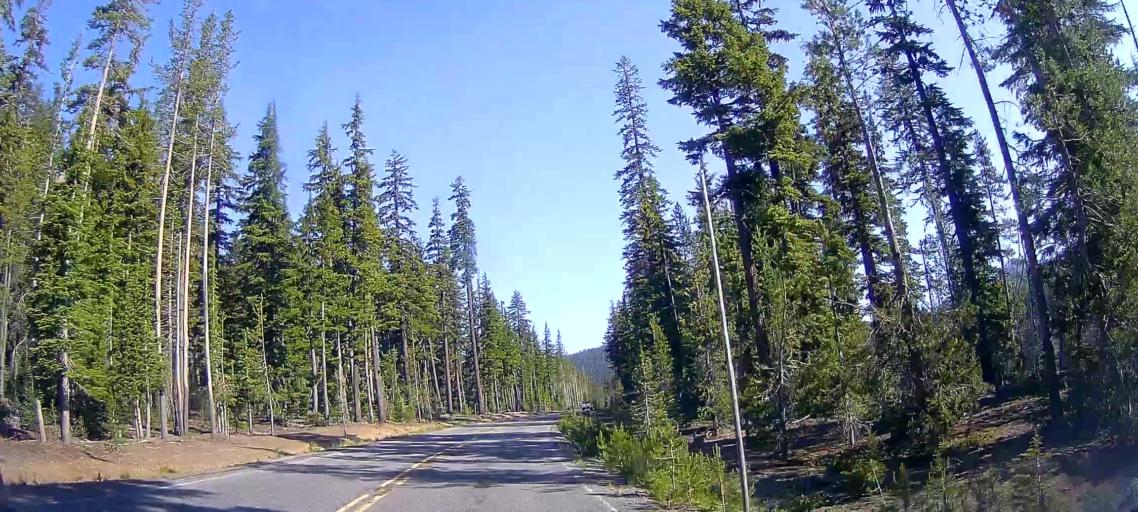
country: US
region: Oregon
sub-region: Jackson County
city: Shady Cove
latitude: 42.8540
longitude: -122.1526
